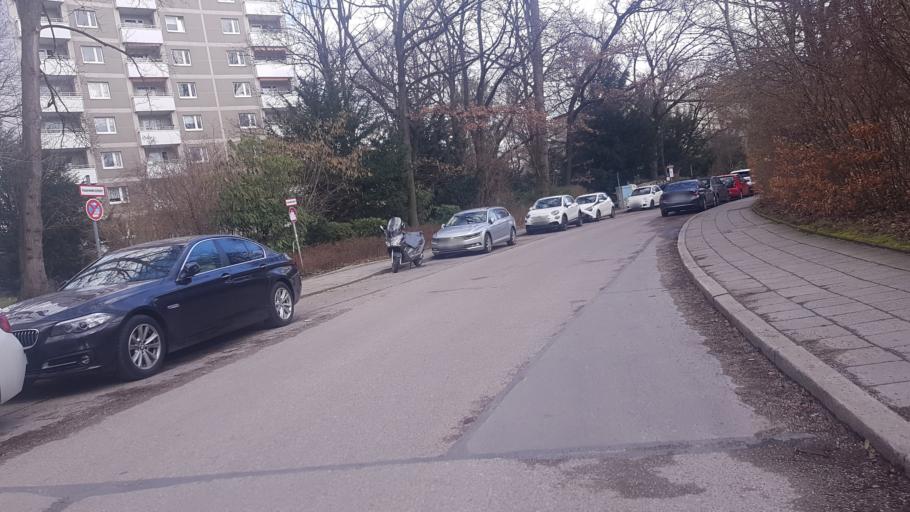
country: DE
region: Bavaria
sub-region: Upper Bavaria
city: Bogenhausen
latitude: 48.1440
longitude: 11.6179
